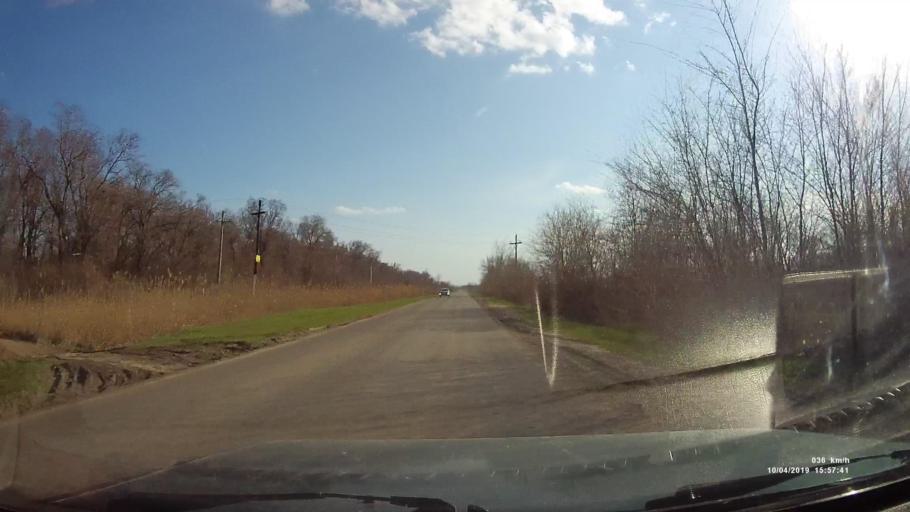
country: RU
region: Rostov
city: Masalovka
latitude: 48.4091
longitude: 40.2751
